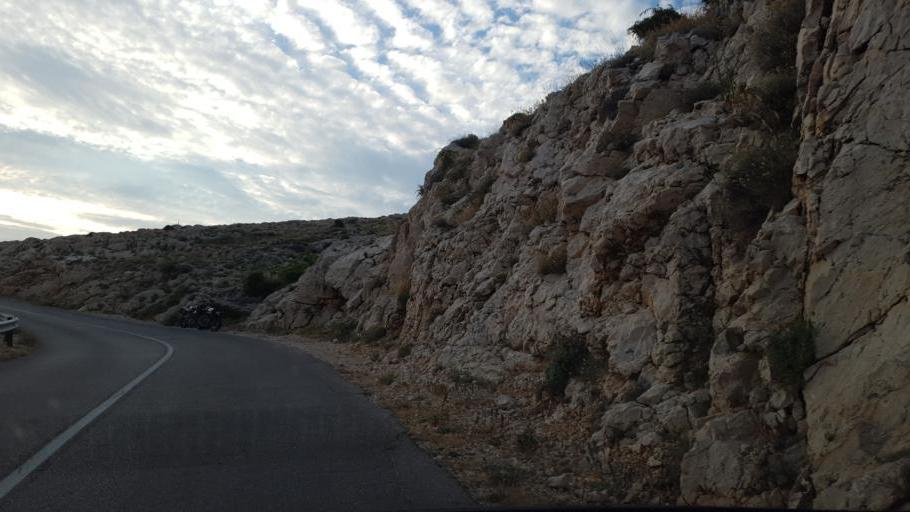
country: HR
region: Primorsko-Goranska
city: Punat
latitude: 44.9742
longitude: 14.6595
